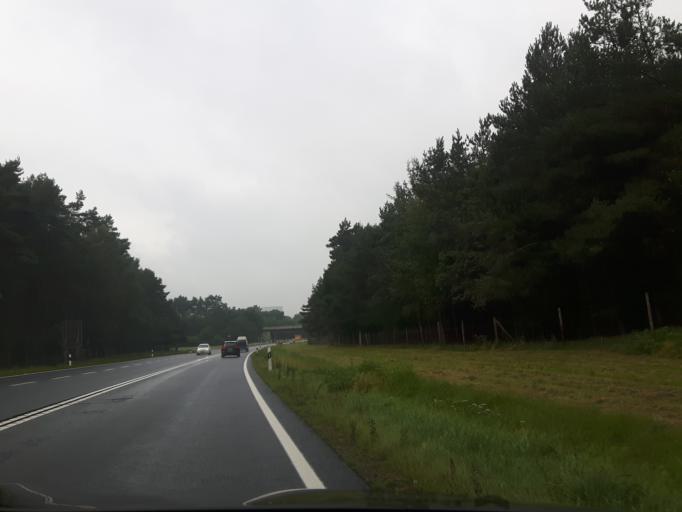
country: DE
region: Lower Saxony
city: Lingen
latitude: 52.4964
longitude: 7.3342
